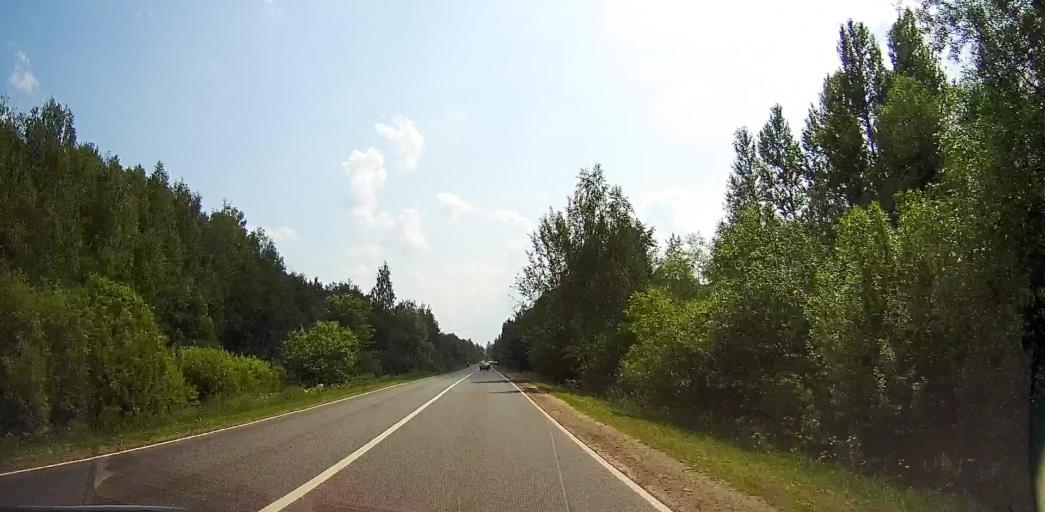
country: RU
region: Moskovskaya
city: Malino
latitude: 55.0929
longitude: 38.1654
